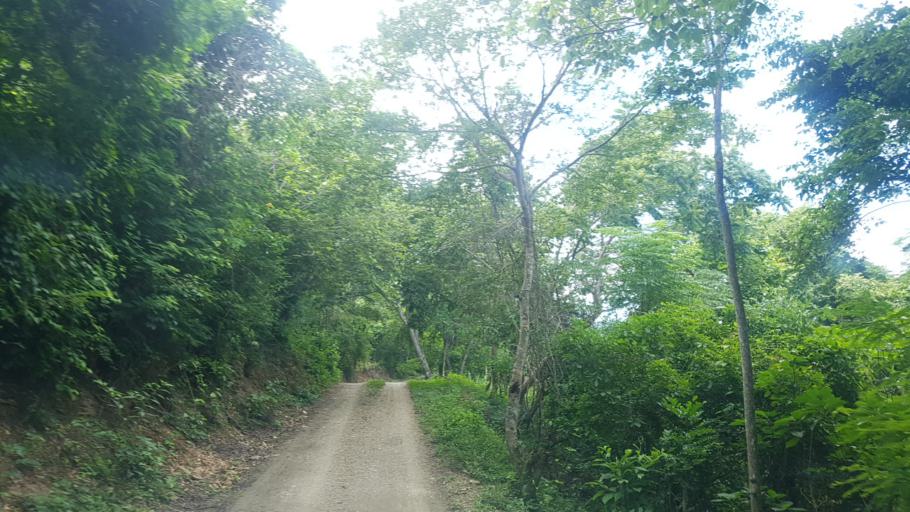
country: NI
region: Nueva Segovia
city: Ocotal
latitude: 13.5947
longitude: -86.4175
